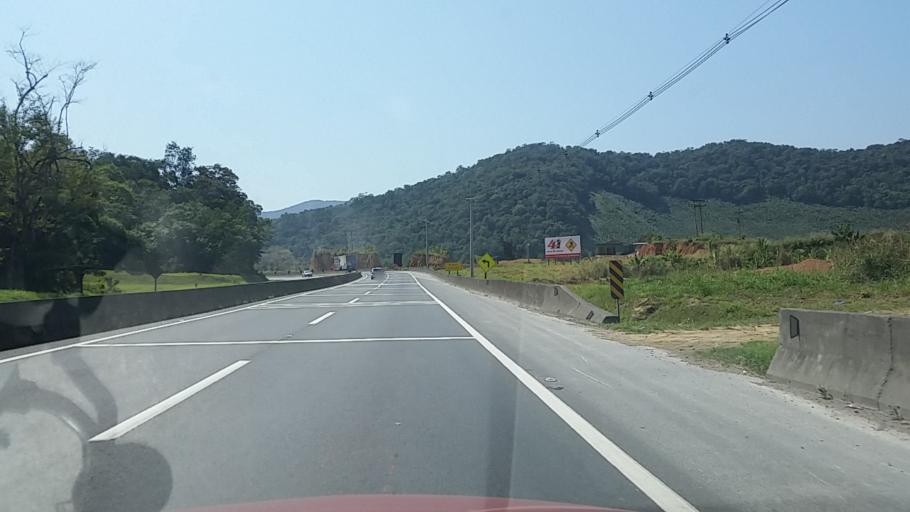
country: BR
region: Sao Paulo
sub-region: Miracatu
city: Miracatu
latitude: -24.1449
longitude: -47.2738
